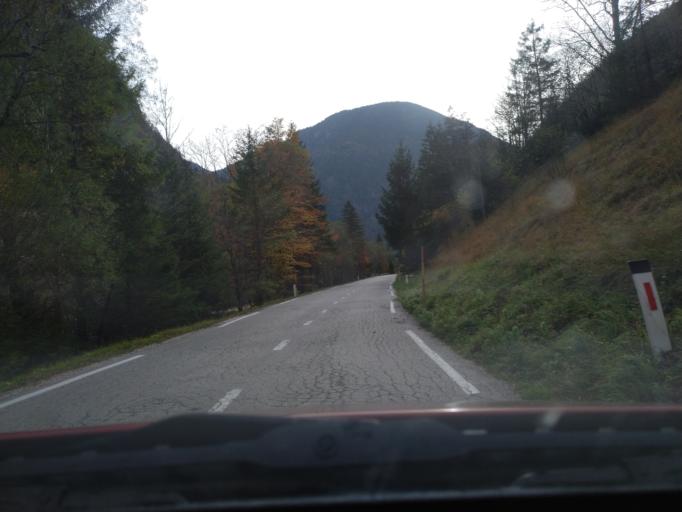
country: SI
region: Kranjska Gora
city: Kranjska Gora
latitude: 46.3509
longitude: 13.6930
